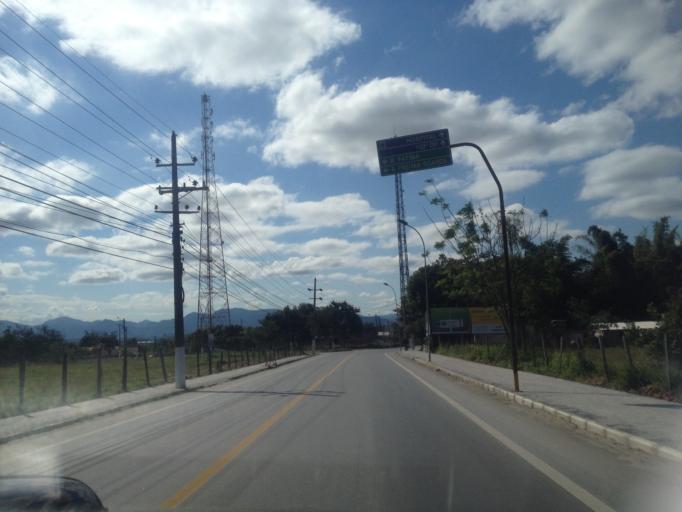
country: BR
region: Rio de Janeiro
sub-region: Porto Real
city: Porto Real
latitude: -22.4484
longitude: -44.3026
